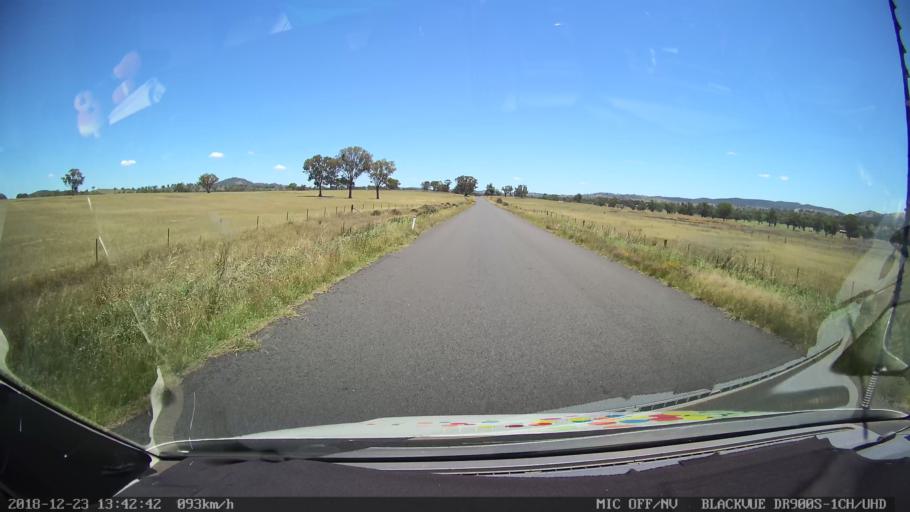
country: AU
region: New South Wales
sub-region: Armidale Dumaresq
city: Armidale
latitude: -30.4797
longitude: 151.1599
